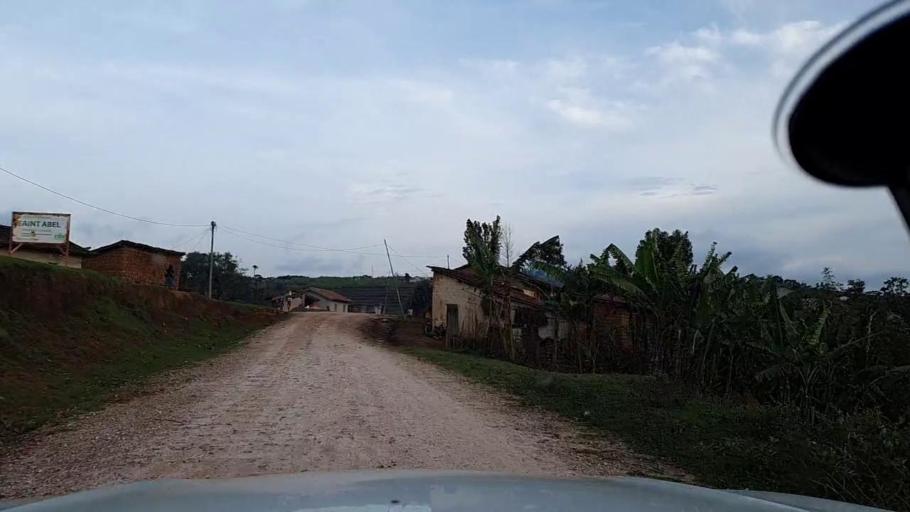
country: RW
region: Southern Province
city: Gitarama
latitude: -2.2076
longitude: 29.6050
